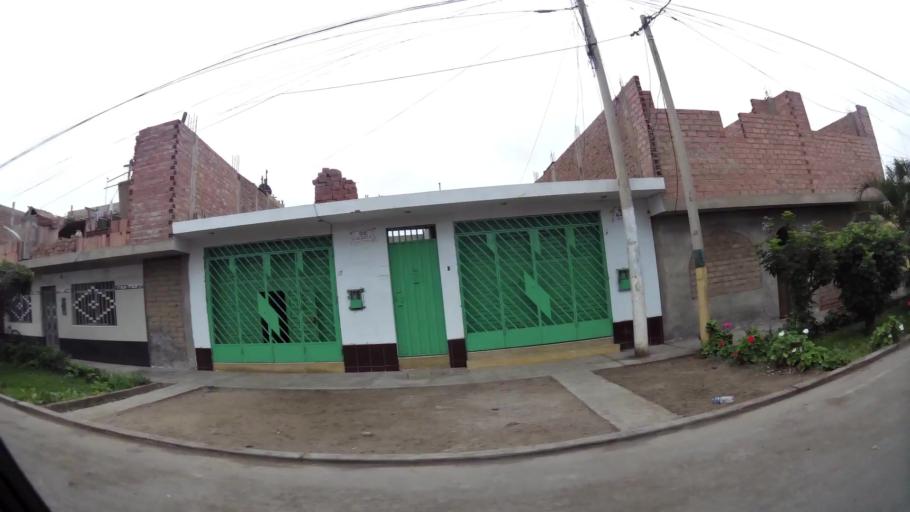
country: PE
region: Lima
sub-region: Barranca
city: Barranca
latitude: -10.7613
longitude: -77.7593
